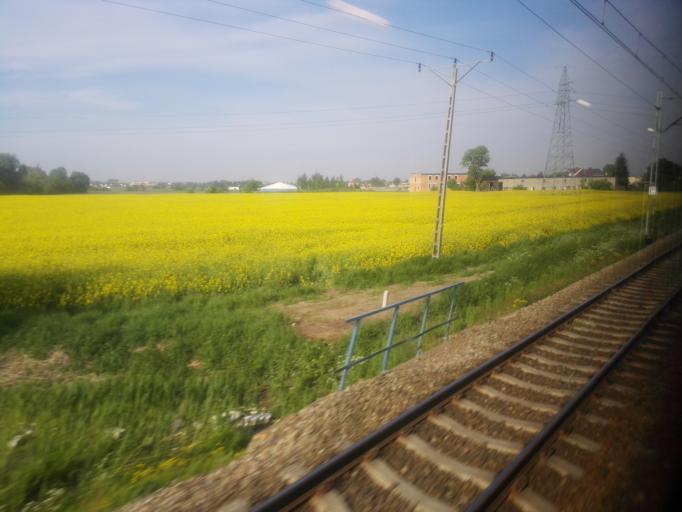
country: PL
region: Greater Poland Voivodeship
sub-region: Powiat wrzesinski
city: Wrzesnia
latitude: 52.3361
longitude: 17.6024
